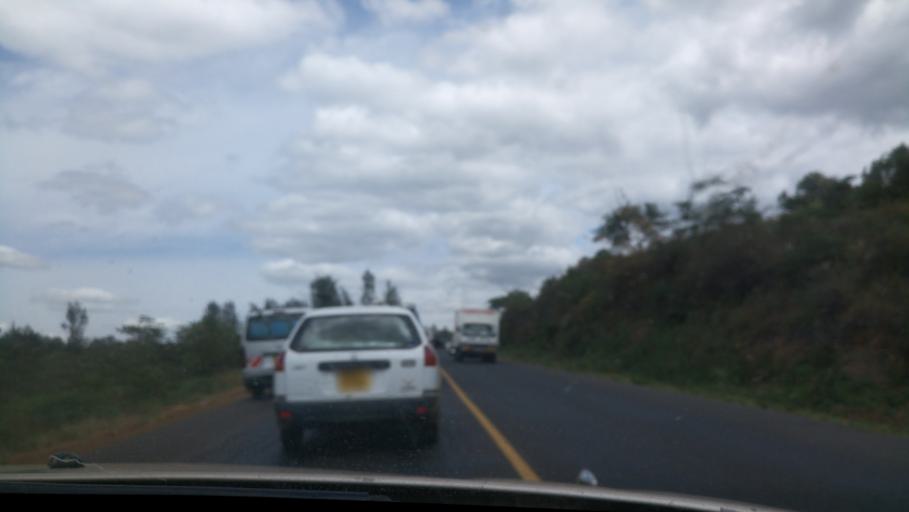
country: KE
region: Murang'a District
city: Maragua
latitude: -0.8495
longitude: 37.2329
